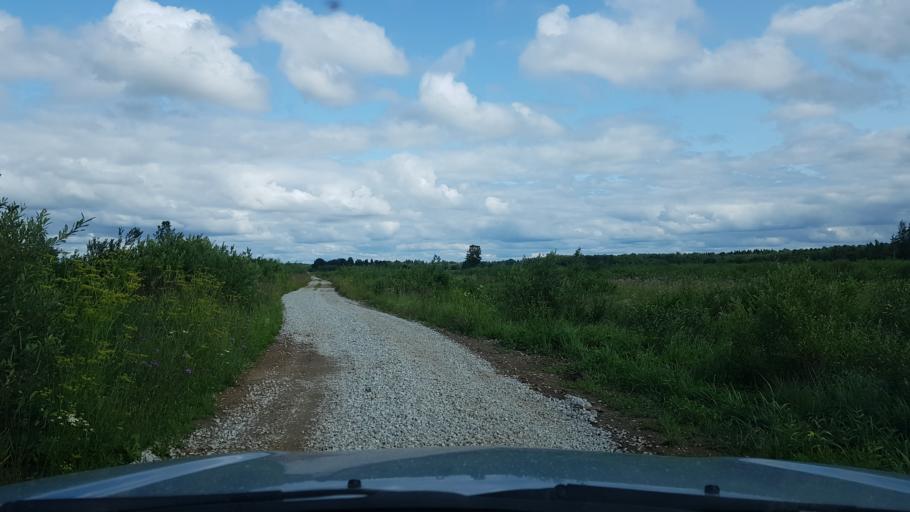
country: EE
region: Ida-Virumaa
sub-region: Narva-Joesuu linn
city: Narva-Joesuu
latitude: 59.3702
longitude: 27.9296
